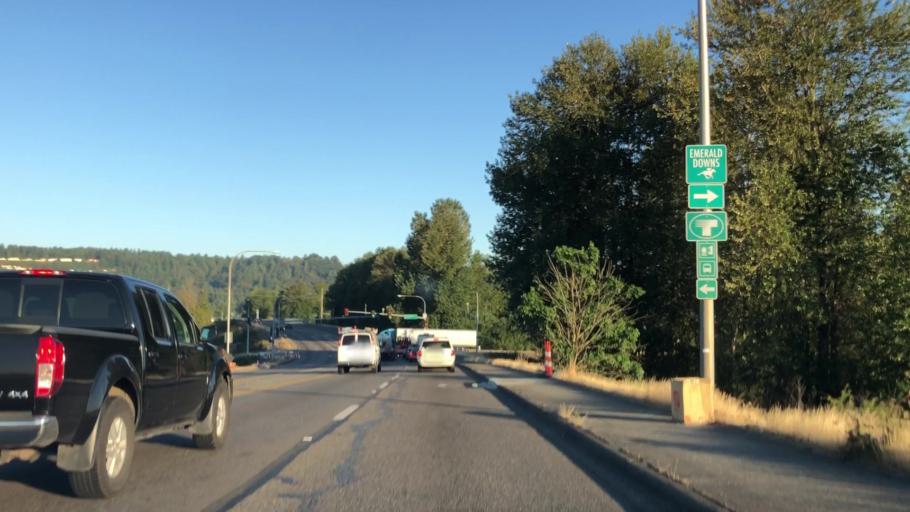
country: US
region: Washington
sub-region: King County
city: Auburn
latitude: 47.3216
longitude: -122.2338
